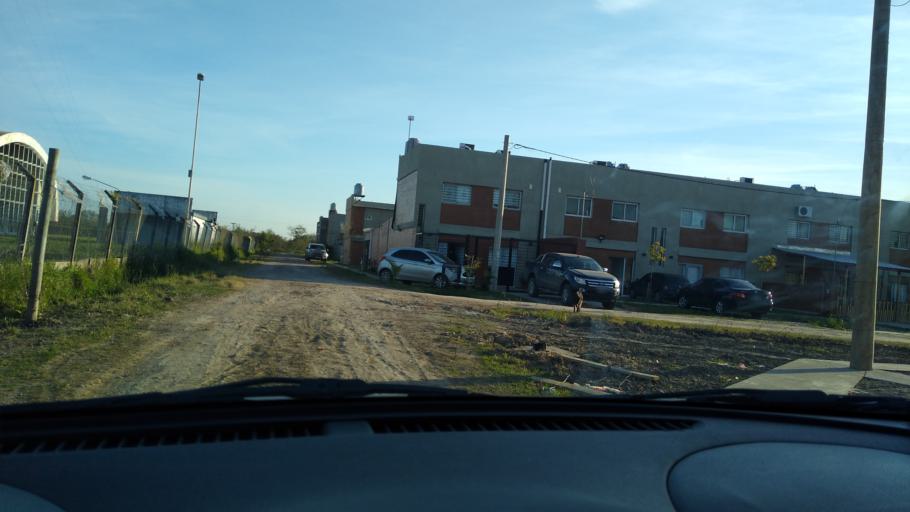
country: AR
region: Chaco
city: Fontana
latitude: -27.4064
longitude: -58.9845
